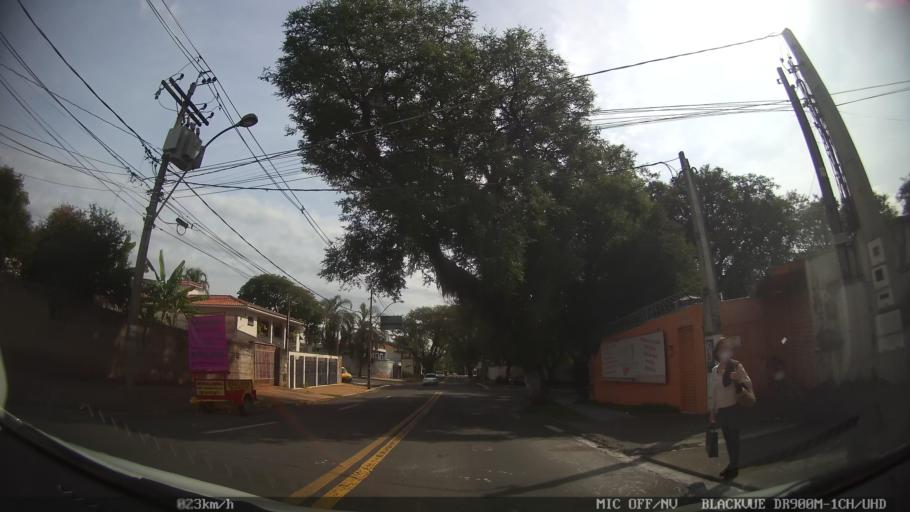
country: BR
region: Sao Paulo
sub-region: Piracicaba
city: Piracicaba
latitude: -22.7169
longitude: -47.6623
